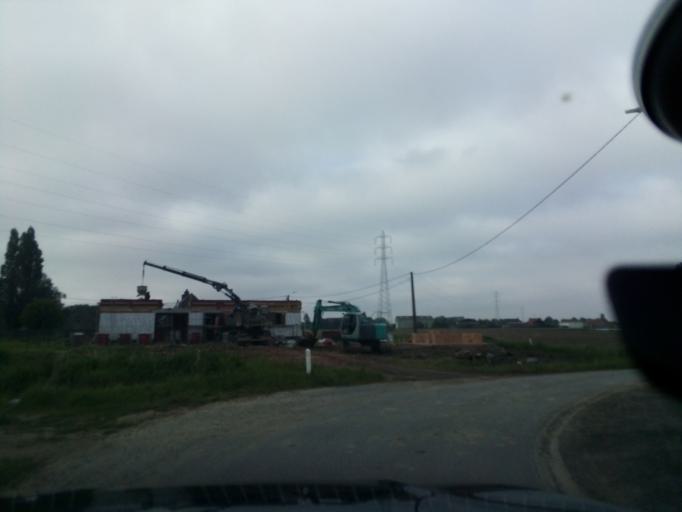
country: BE
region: Flanders
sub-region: Provincie West-Vlaanderen
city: Ingelmunster
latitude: 50.9396
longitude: 3.2414
